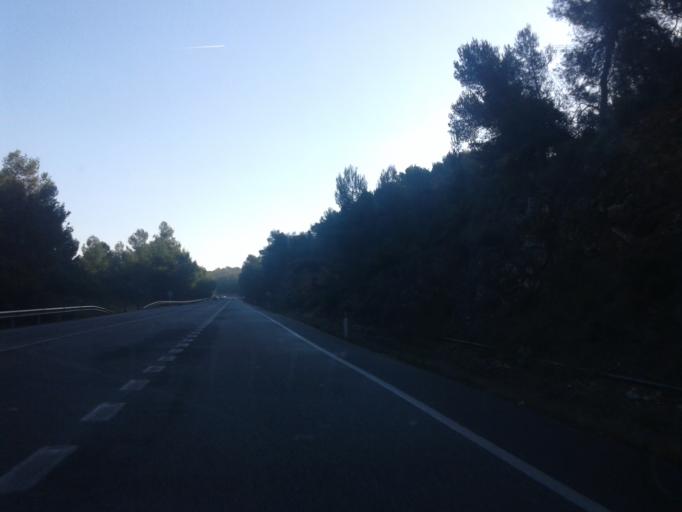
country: ES
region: Catalonia
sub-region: Provincia de Barcelona
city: Subirats
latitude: 41.3887
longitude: 1.8175
